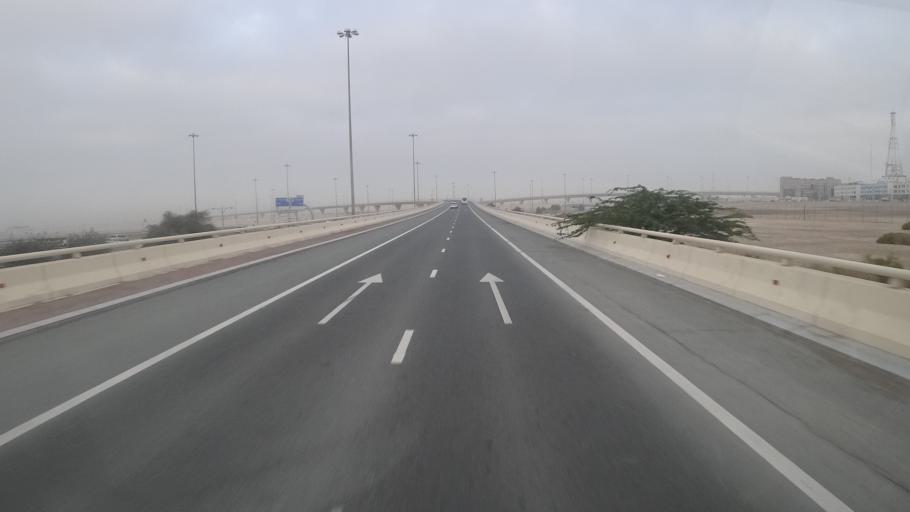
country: AE
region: Abu Dhabi
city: Abu Dhabi
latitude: 24.3065
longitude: 54.6080
